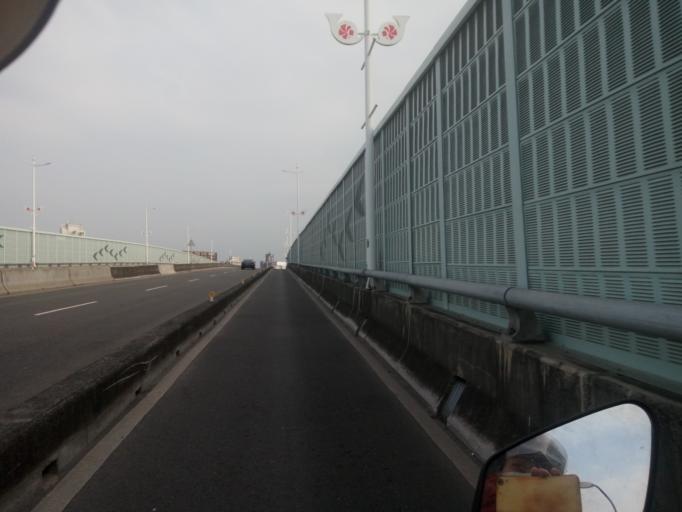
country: TW
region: Taiwan
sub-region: Chiayi
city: Jiayi Shi
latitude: 23.4765
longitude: 120.4319
